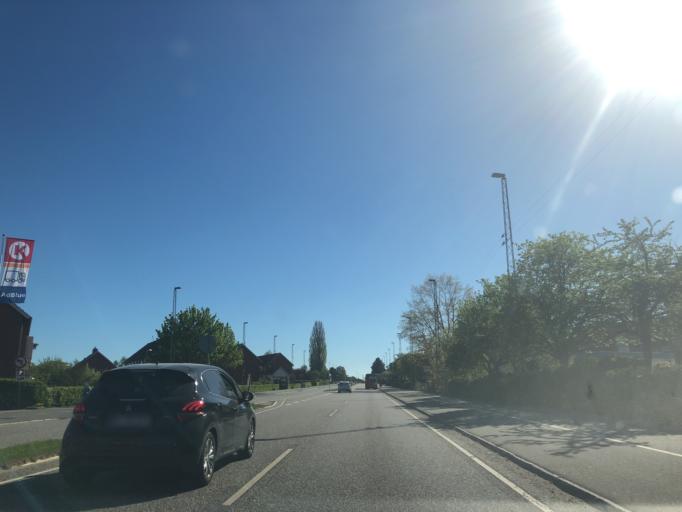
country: DK
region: Zealand
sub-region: Koge Kommune
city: Koge
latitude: 55.4468
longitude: 12.1727
